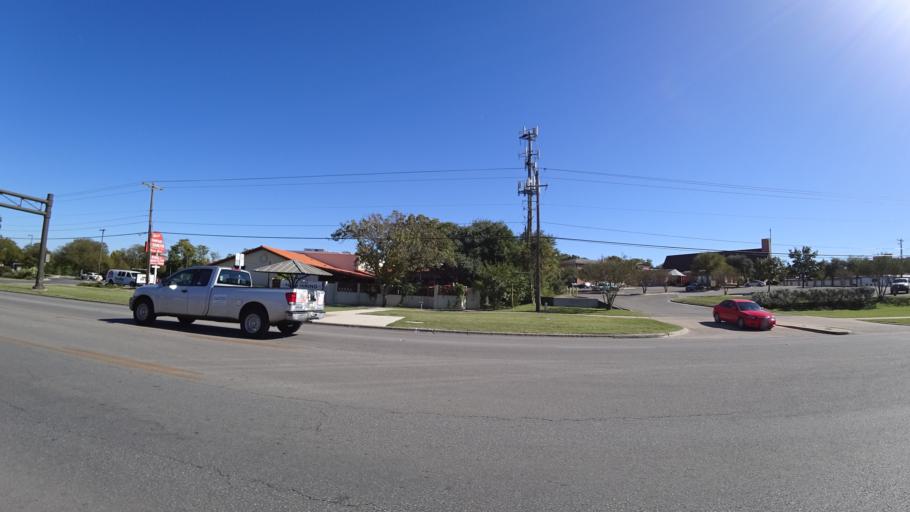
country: US
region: Texas
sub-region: Travis County
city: Rollingwood
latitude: 30.2454
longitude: -97.7799
